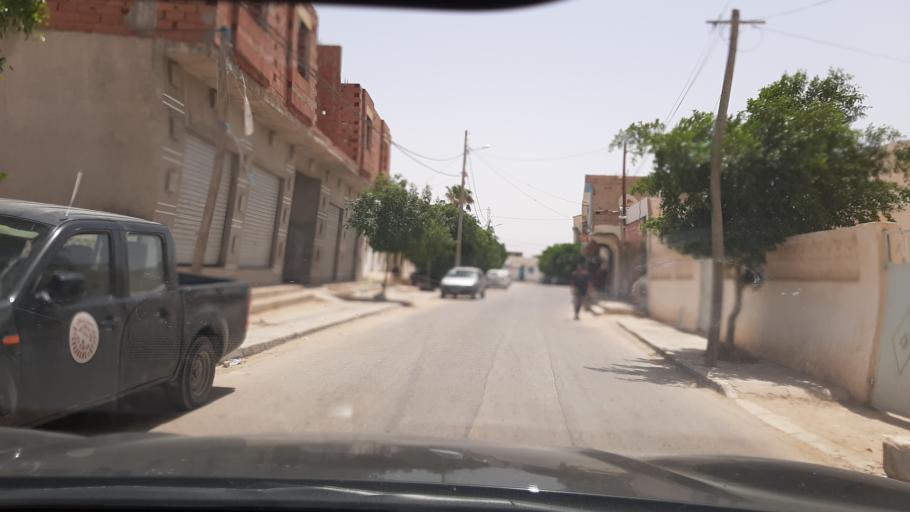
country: TN
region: Qabis
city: Matmata
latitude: 33.6167
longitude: 10.2869
